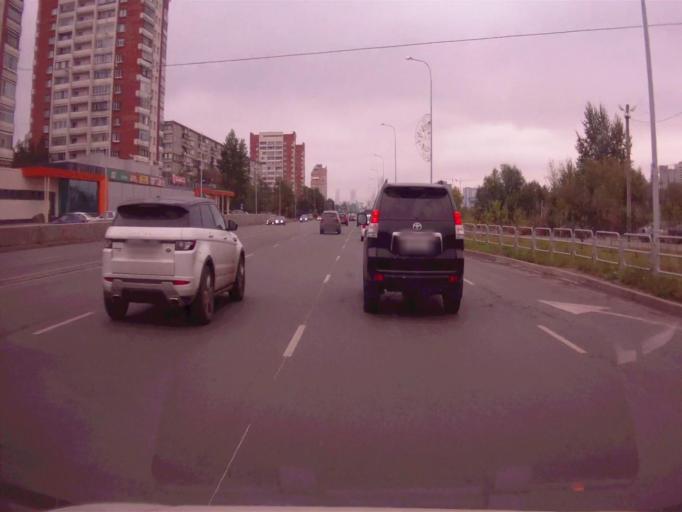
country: RU
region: Chelyabinsk
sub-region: Gorod Chelyabinsk
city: Chelyabinsk
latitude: 55.1745
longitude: 61.3450
